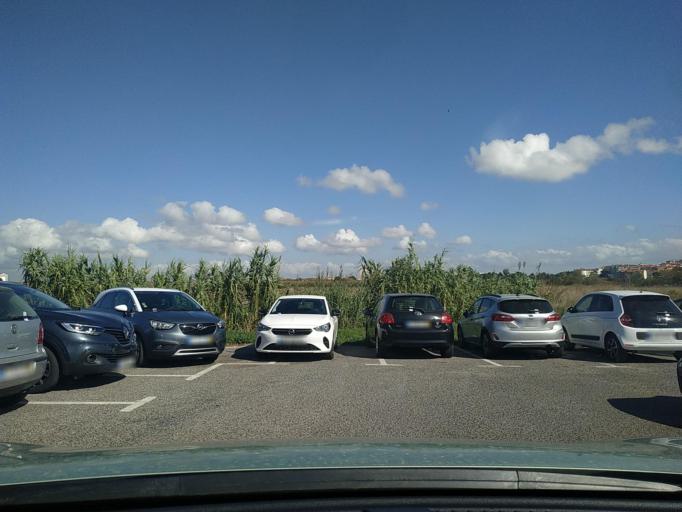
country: PT
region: Lisbon
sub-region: Amadora
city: Amadora
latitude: 38.7595
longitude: -9.2177
